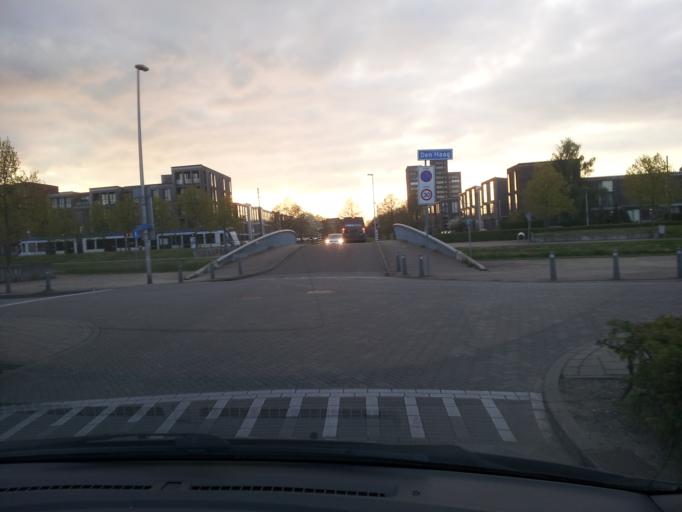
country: NL
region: South Holland
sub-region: Gemeente Den Haag
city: Ypenburg
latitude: 52.0447
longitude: 4.3784
